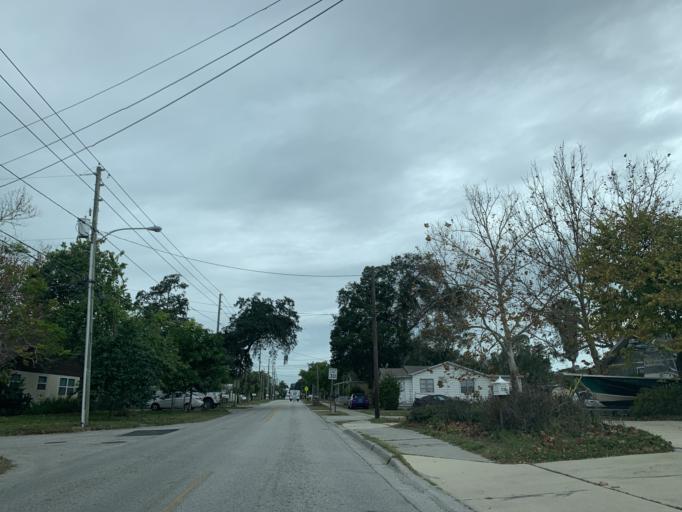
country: US
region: Florida
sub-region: Pinellas County
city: Belleair
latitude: 27.9352
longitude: -82.7893
